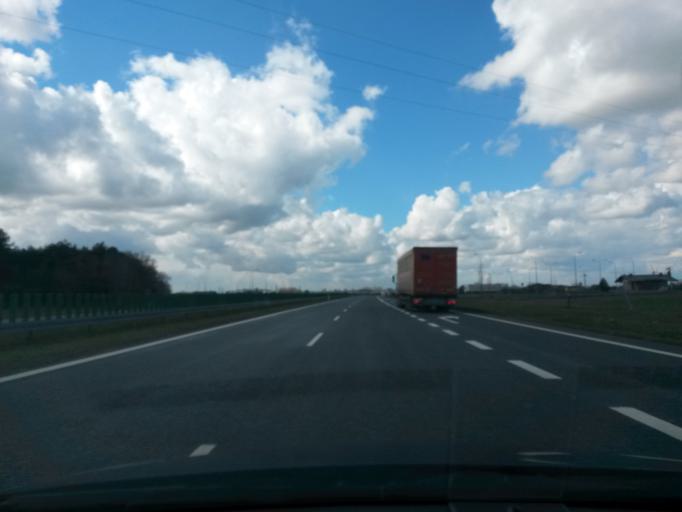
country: PL
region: Lodz Voivodeship
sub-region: Powiat leczycki
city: Swinice Warckie
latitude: 52.0338
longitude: 18.8819
